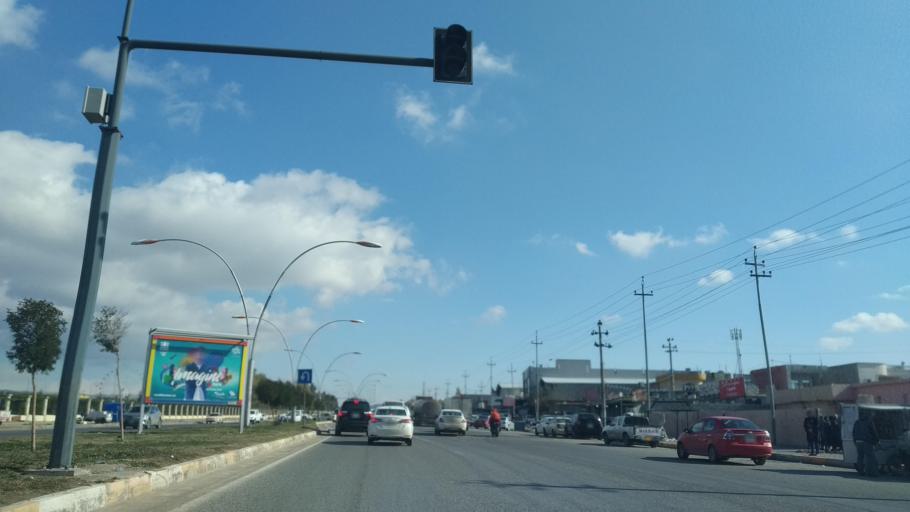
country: IQ
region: Arbil
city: Erbil
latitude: 36.2077
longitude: 44.1360
